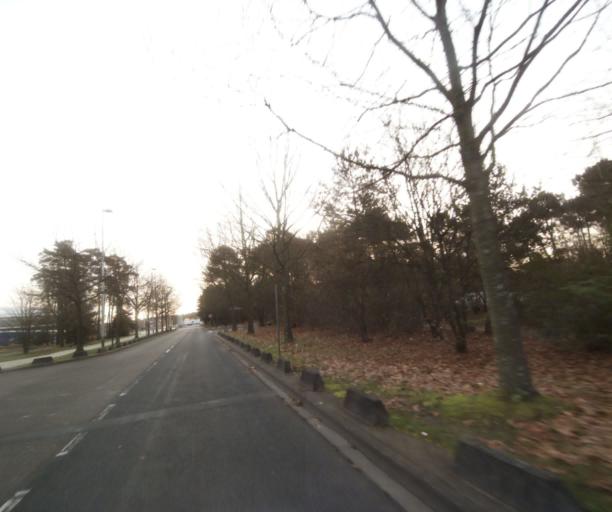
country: FR
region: Pays de la Loire
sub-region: Departement de la Sarthe
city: Ruaudin
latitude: 47.9556
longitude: 0.2233
